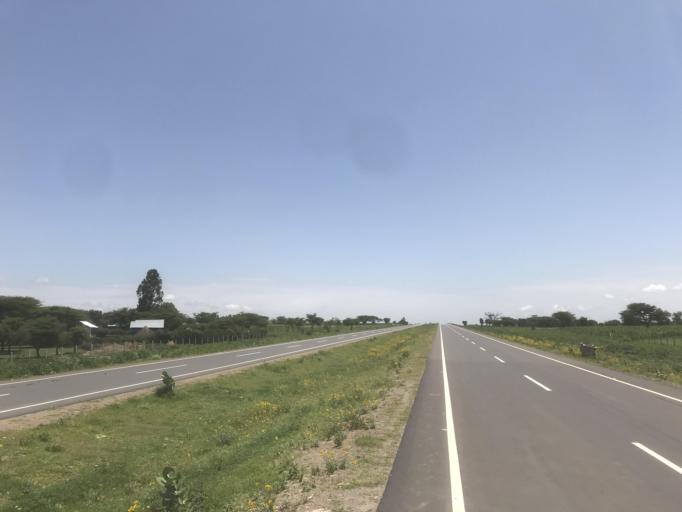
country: ET
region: Oromiya
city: Mojo
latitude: 8.3686
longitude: 38.9953
